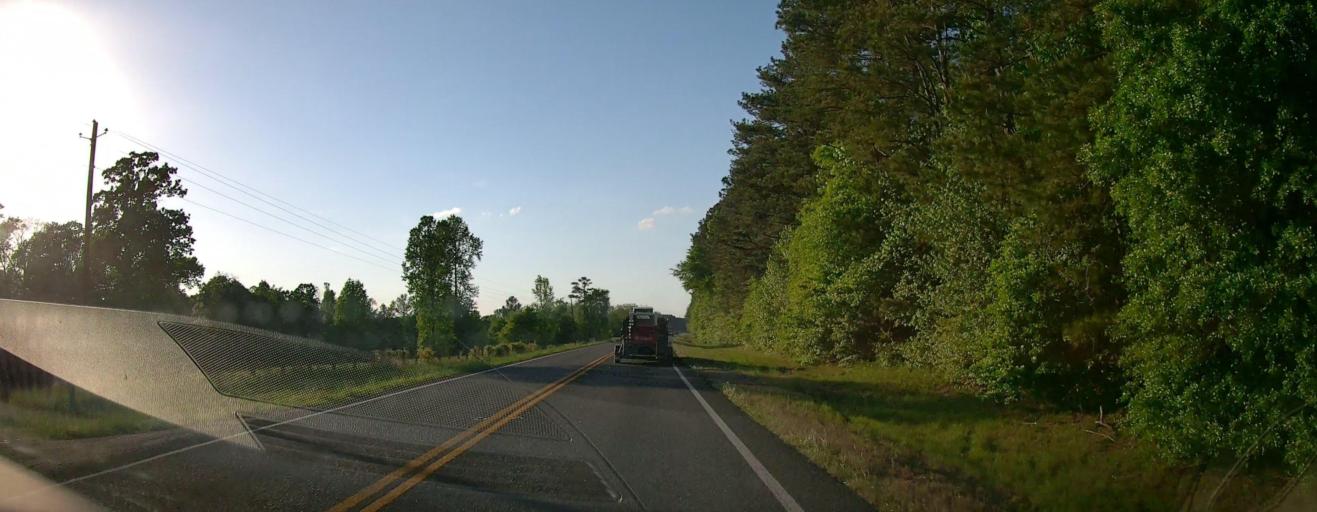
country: US
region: Georgia
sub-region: Jasper County
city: Monticello
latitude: 33.4174
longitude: -83.6104
